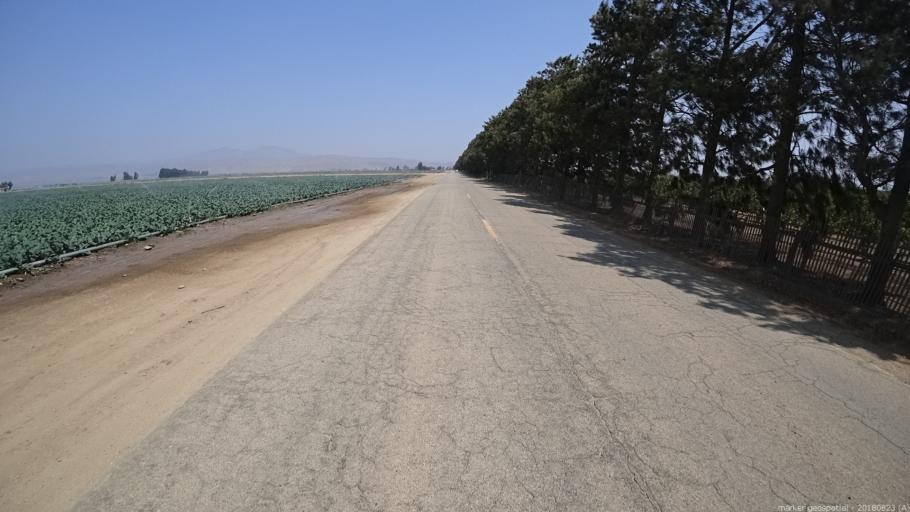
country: US
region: California
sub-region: Monterey County
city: Greenfield
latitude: 36.3311
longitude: -121.2740
